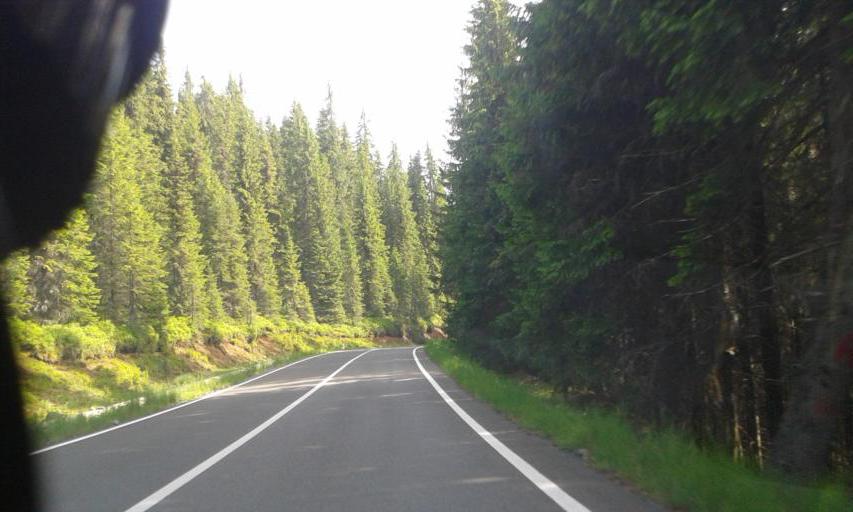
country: RO
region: Hunedoara
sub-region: Oras Petrila
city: Petrila
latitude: 45.4954
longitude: 23.6384
